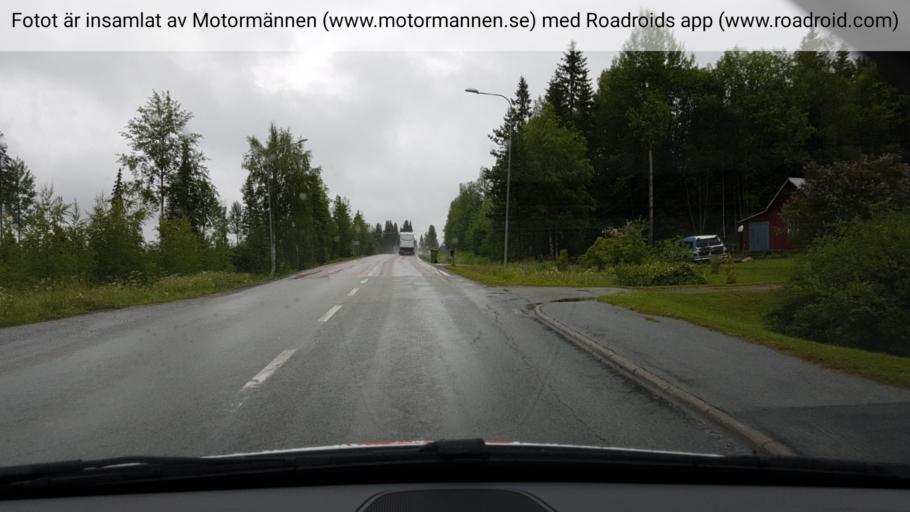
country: SE
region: Jaemtland
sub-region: Stroemsunds Kommun
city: Stroemsund
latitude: 63.8626
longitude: 15.5692
